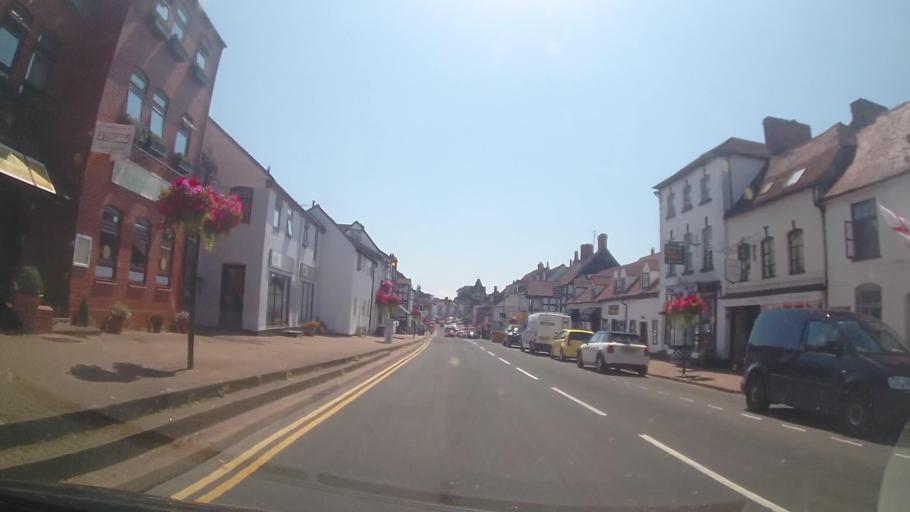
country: GB
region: England
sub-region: Herefordshire
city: Ledbury
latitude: 52.0398
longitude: -2.4238
